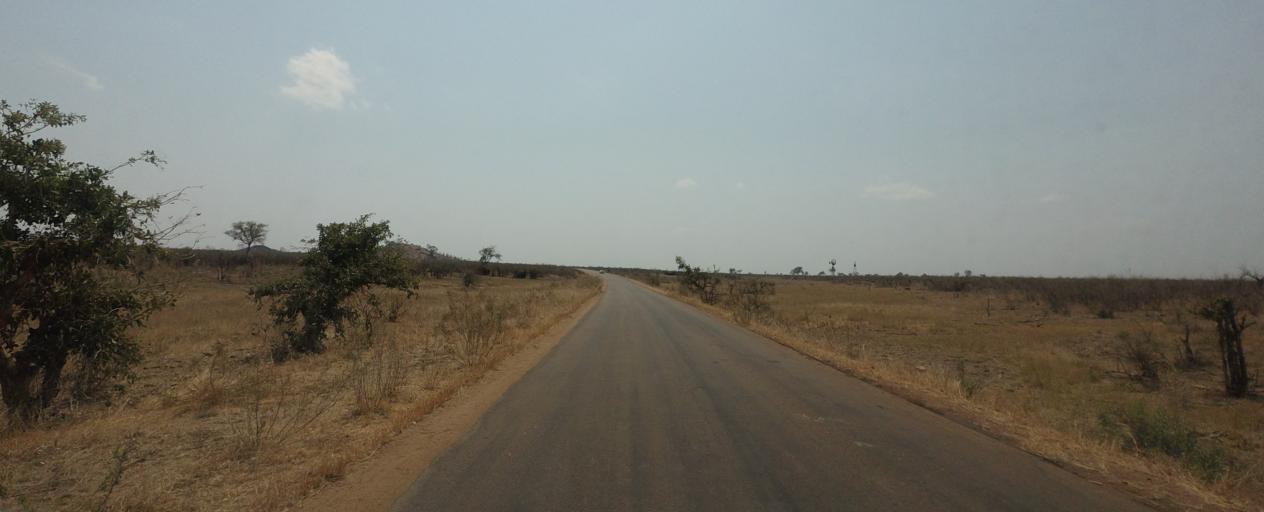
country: ZA
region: Limpopo
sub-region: Mopani District Municipality
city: Phalaborwa
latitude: -23.5001
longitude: 31.4020
